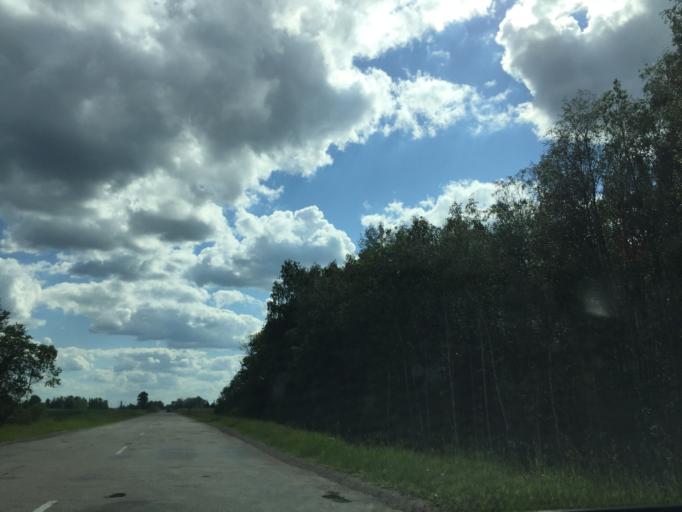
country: LV
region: Jaunpils
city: Jaunpils
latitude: 56.8622
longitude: 23.0562
